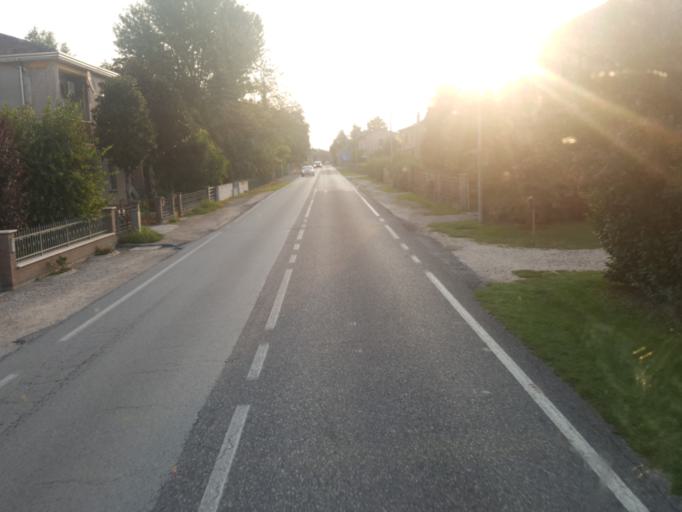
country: IT
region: Emilia-Romagna
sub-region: Provincia di Ravenna
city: Lavezzola
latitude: 44.5581
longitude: 11.8720
